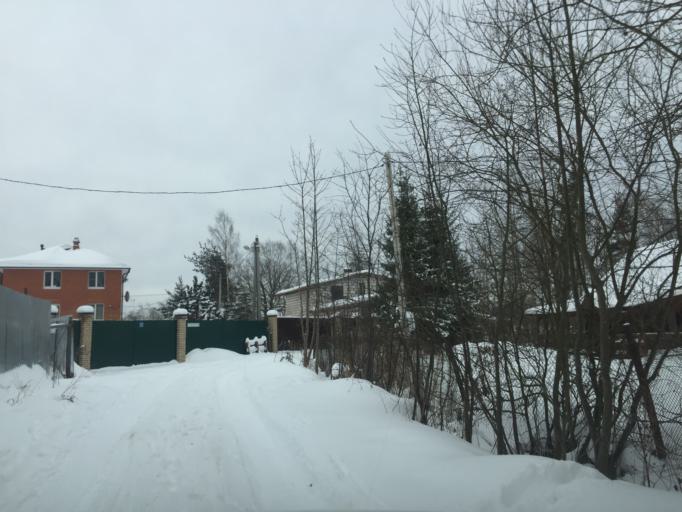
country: RU
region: Leningrad
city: Otradnoye
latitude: 59.7798
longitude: 30.7868
